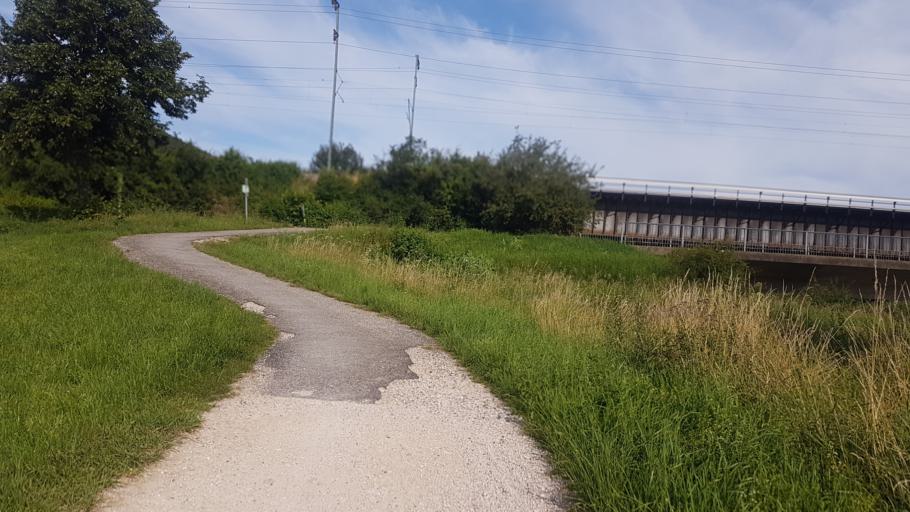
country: DE
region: Bavaria
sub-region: Regierungsbezirk Mittelfranken
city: Treuchtlingen
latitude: 48.9730
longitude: 10.9155
